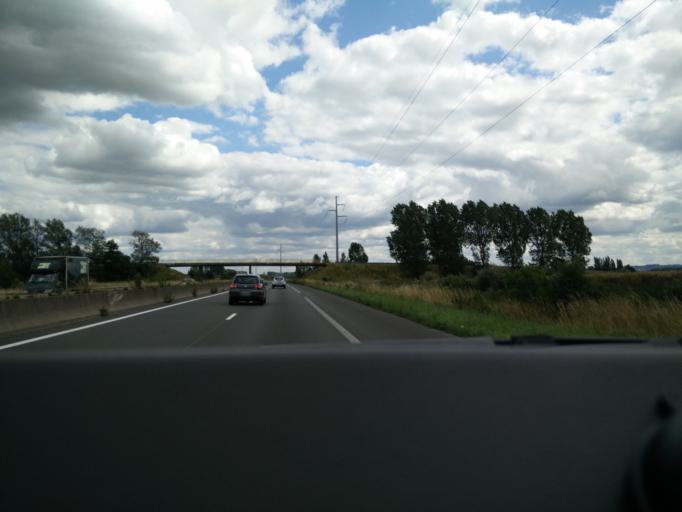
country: FR
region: Nord-Pas-de-Calais
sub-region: Departement du Nord
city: Wormhout
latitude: 50.9089
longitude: 2.4862
